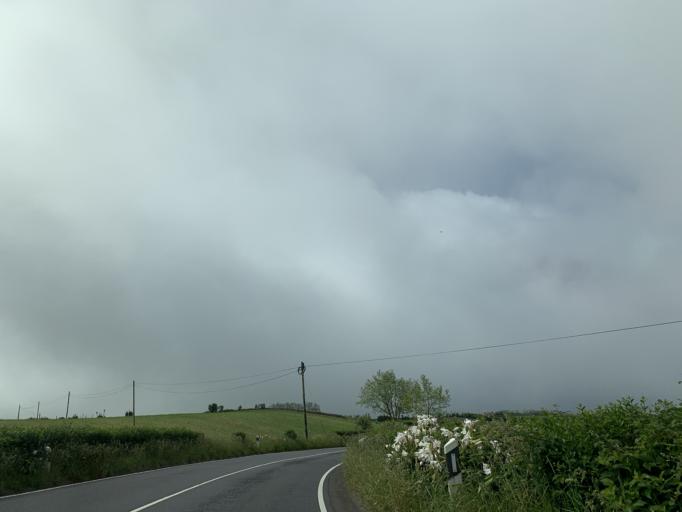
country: PT
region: Azores
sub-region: Ponta Delgada
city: Arrifes
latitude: 37.7724
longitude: -25.7412
